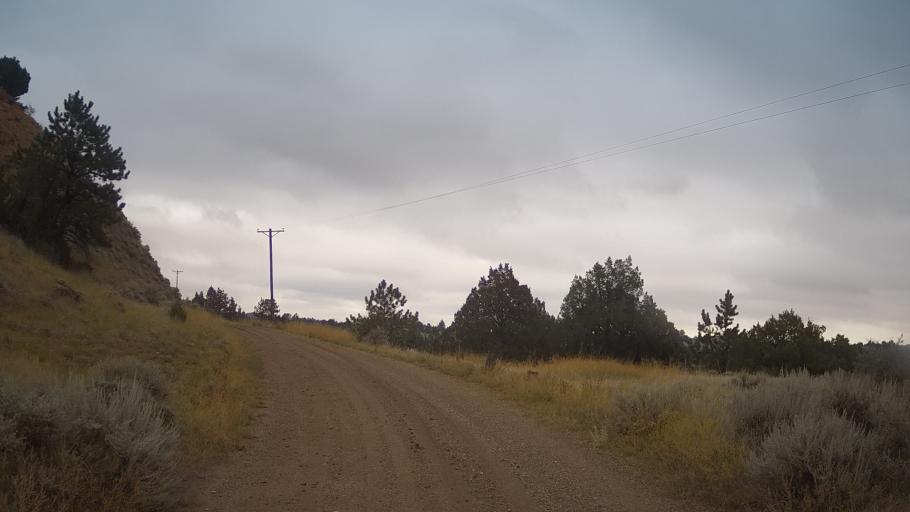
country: US
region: Montana
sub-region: Dawson County
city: Glendive
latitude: 47.0430
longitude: -104.6750
